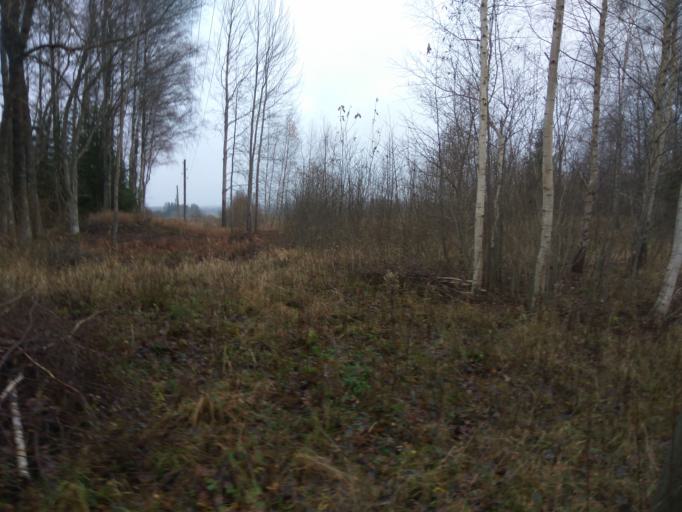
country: LV
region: Kuldigas Rajons
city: Kuldiga
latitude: 56.9316
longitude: 22.0068
